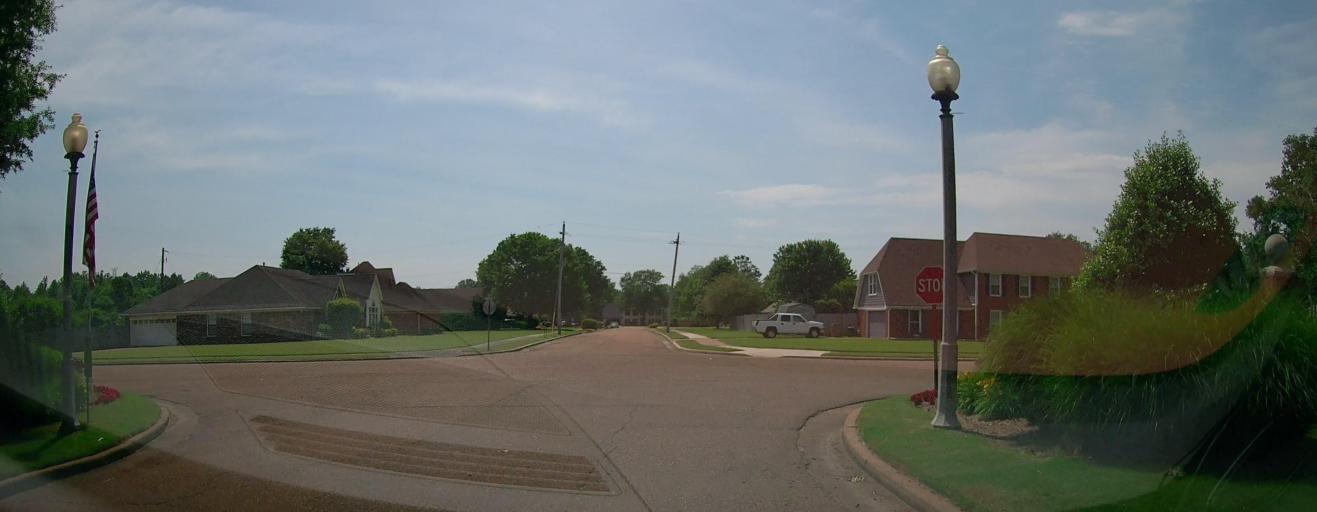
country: US
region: Tennessee
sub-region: Shelby County
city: Germantown
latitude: 35.0395
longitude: -89.7867
